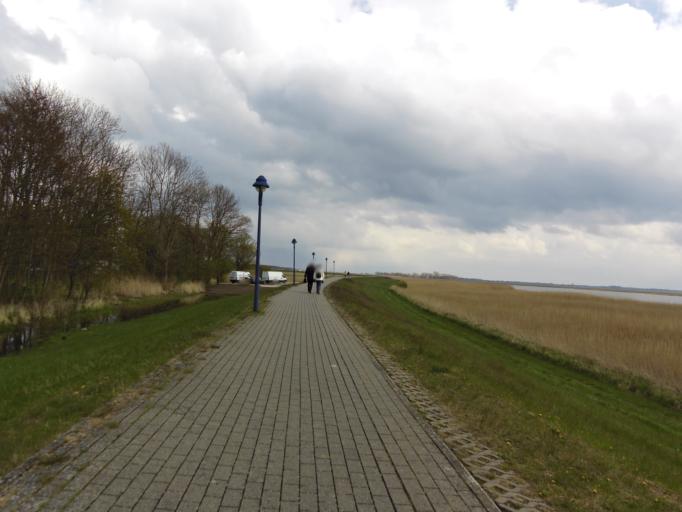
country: DE
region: Mecklenburg-Vorpommern
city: Zingst
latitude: 54.4310
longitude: 12.7047
